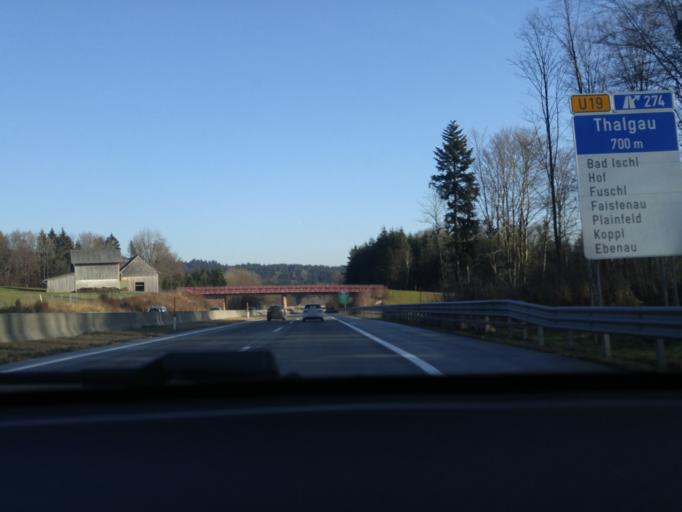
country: AT
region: Salzburg
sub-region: Politischer Bezirk Salzburg-Umgebung
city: Plainfeld
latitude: 47.8556
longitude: 13.2096
